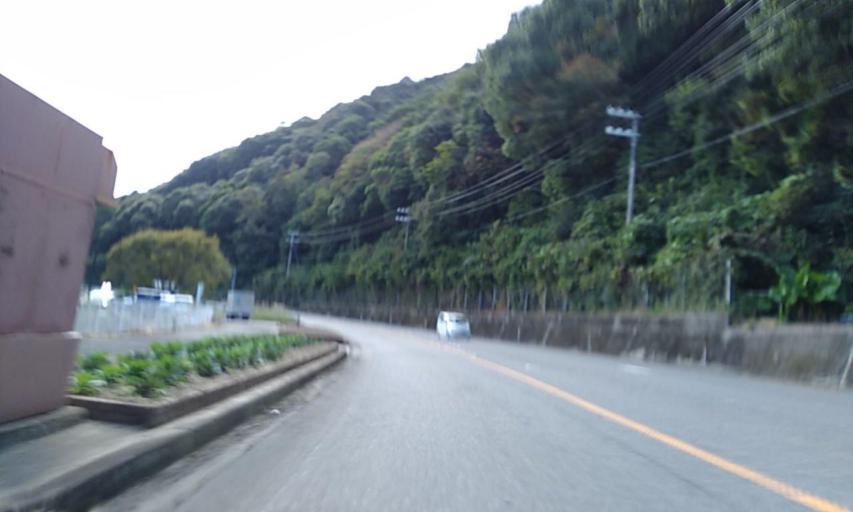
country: JP
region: Wakayama
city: Gobo
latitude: 33.9640
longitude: 135.1229
